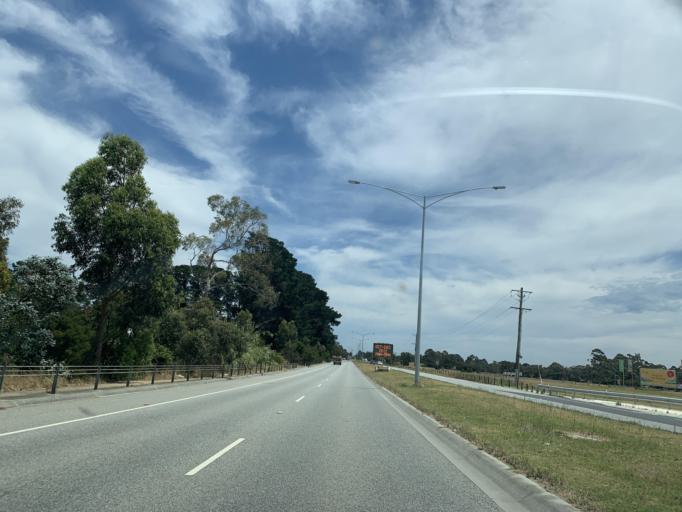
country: AU
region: Victoria
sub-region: Casey
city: Cranbourne South
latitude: -38.1318
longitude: 145.2331
